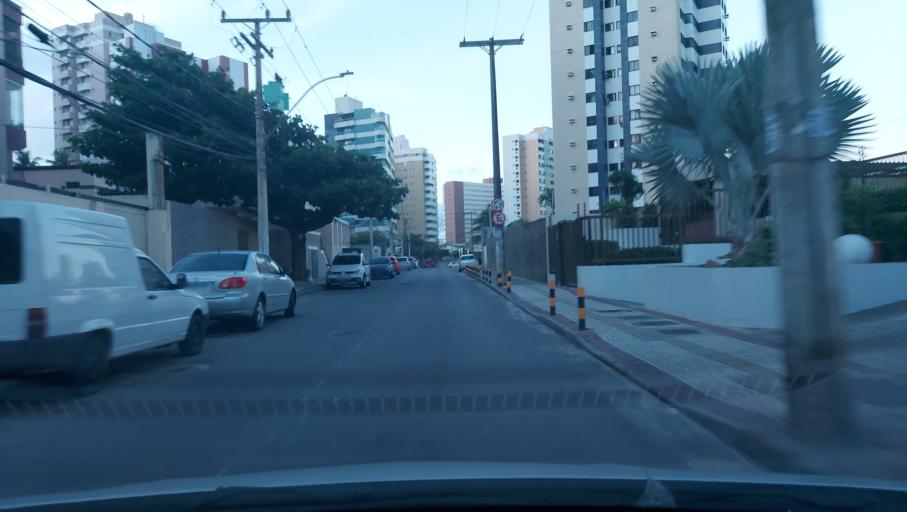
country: BR
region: Bahia
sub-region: Salvador
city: Salvador
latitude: -12.9885
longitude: -38.4387
